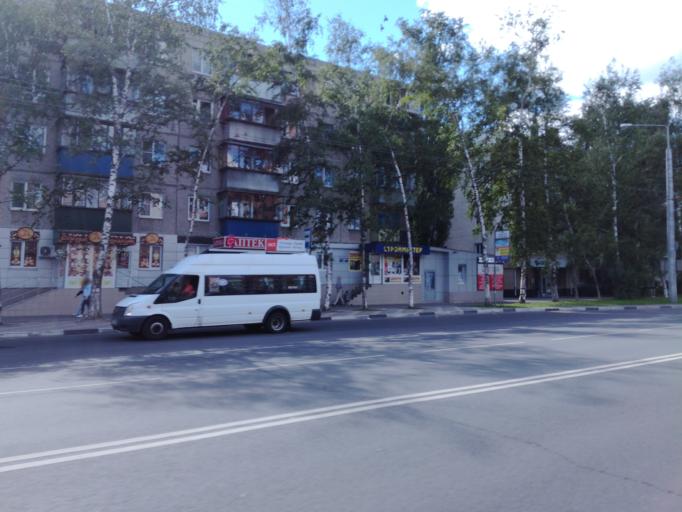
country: RU
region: Kursk
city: Kursk
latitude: 51.7589
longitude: 36.1871
